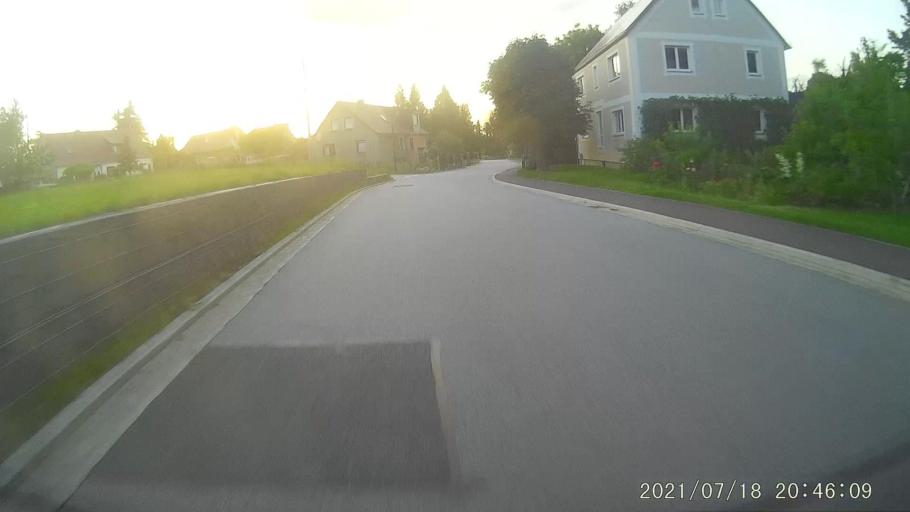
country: DE
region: Saxony
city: Reichenbach
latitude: 51.1917
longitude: 14.7891
